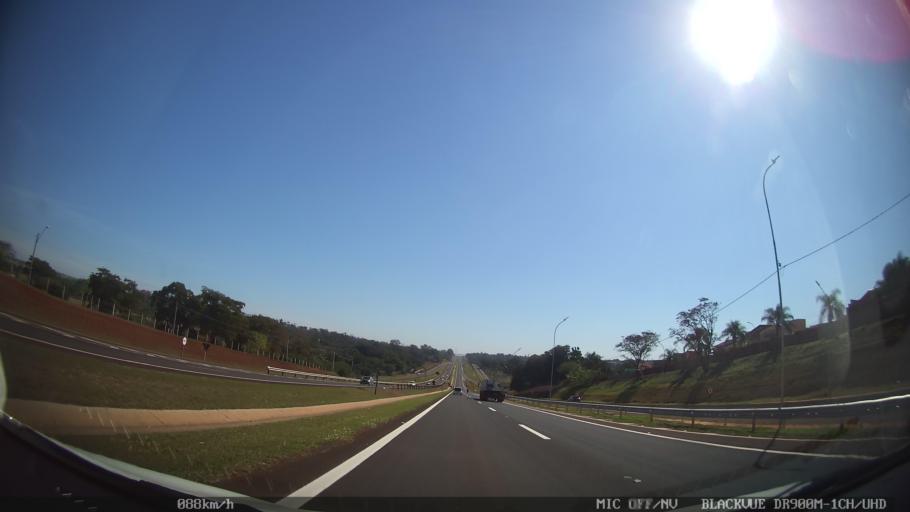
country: BR
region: Sao Paulo
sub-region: Ribeirao Preto
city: Ribeirao Preto
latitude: -21.2175
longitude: -47.8327
